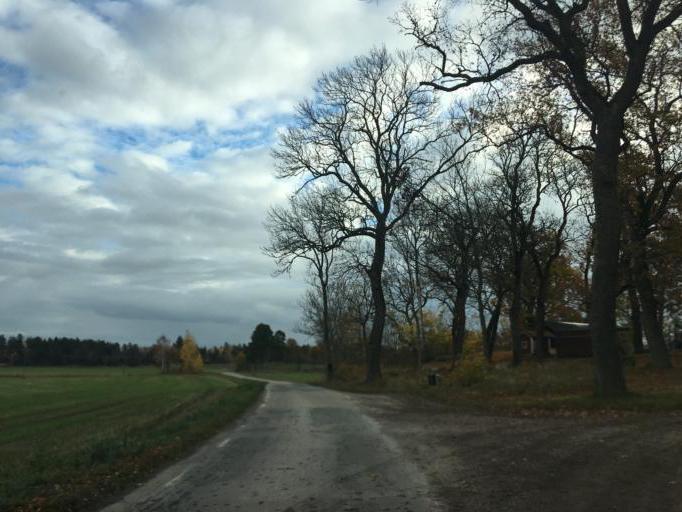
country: SE
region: Vaestmanland
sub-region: Vasteras
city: Vasteras
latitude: 59.5660
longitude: 16.4139
